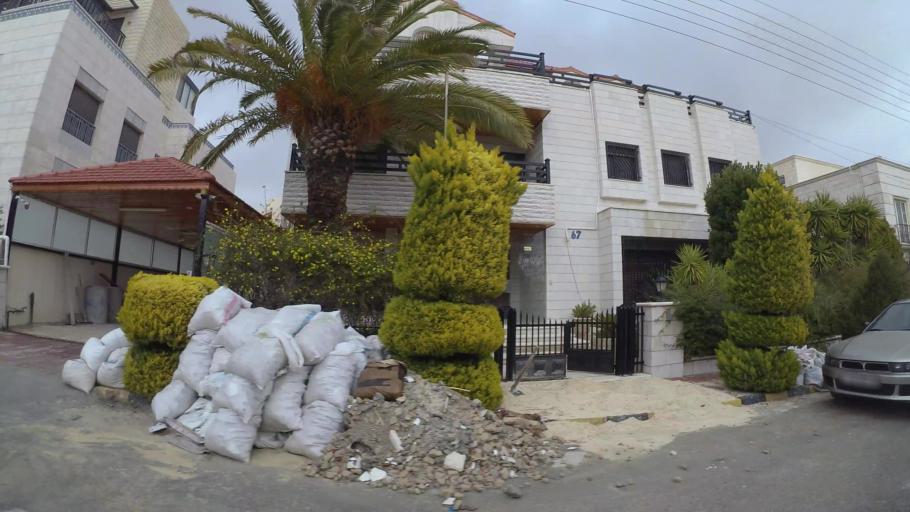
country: JO
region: Amman
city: Al Bunayyat ash Shamaliyah
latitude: 31.9504
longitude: 35.8801
